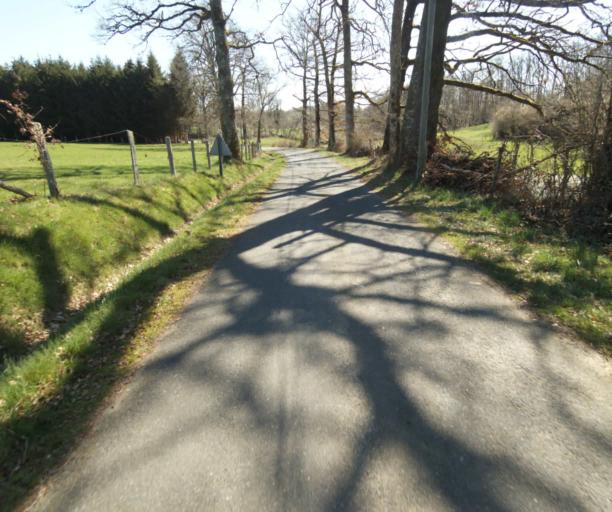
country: FR
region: Limousin
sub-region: Departement de la Correze
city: Saint-Mexant
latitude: 45.3107
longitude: 1.6432
